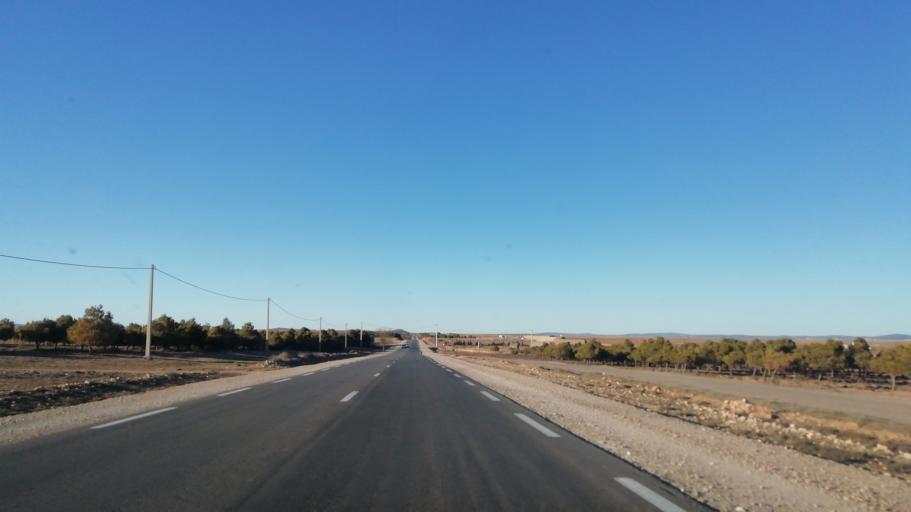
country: DZ
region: Tlemcen
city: Sebdou
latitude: 34.5043
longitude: -1.2791
